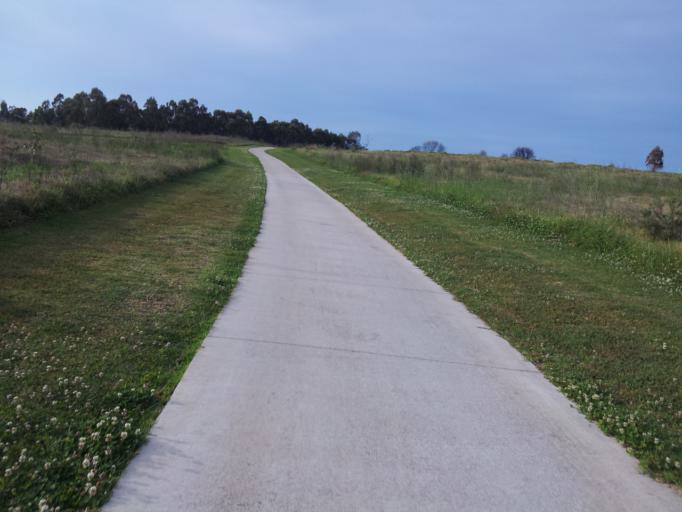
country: AU
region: New South Wales
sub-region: Fairfield
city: Horsley Park
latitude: -33.8548
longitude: 150.8723
